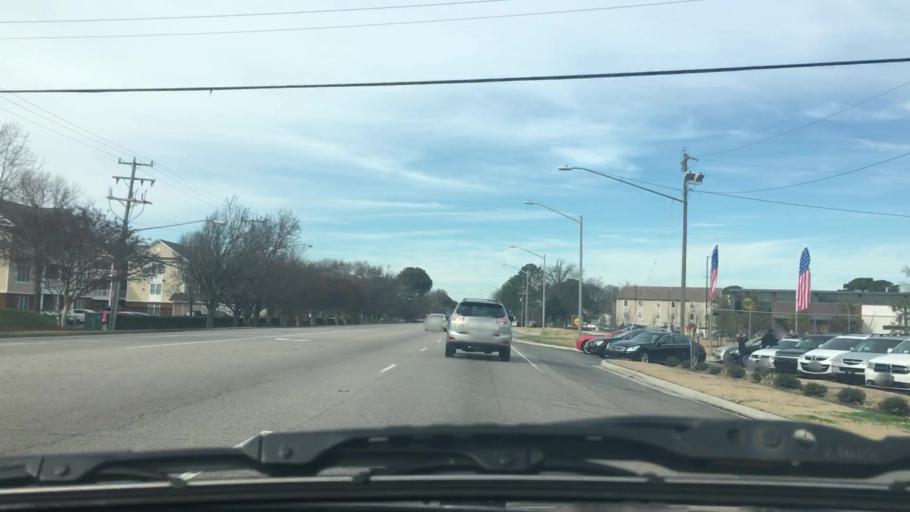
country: US
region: Virginia
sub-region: City of Norfolk
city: Norfolk
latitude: 36.8985
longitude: -76.2262
